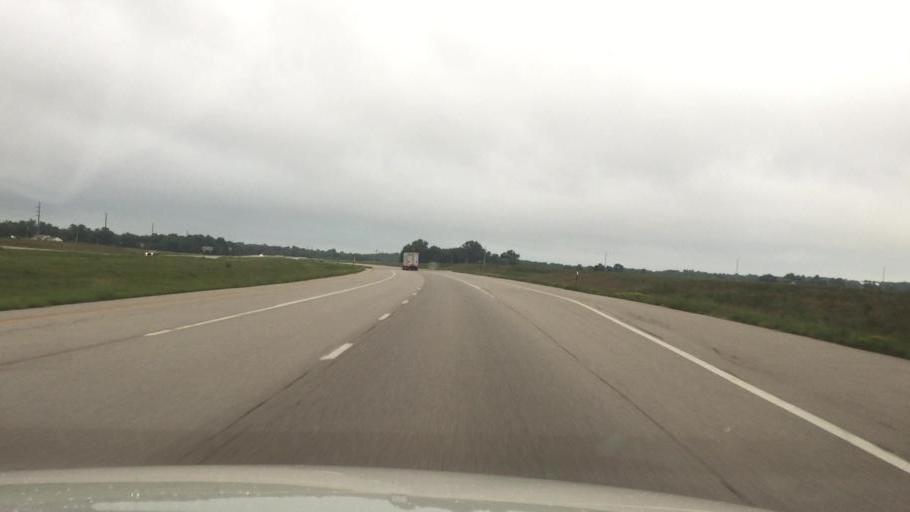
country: US
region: Kansas
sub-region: Montgomery County
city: Coffeyville
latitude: 37.0758
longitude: -95.5893
